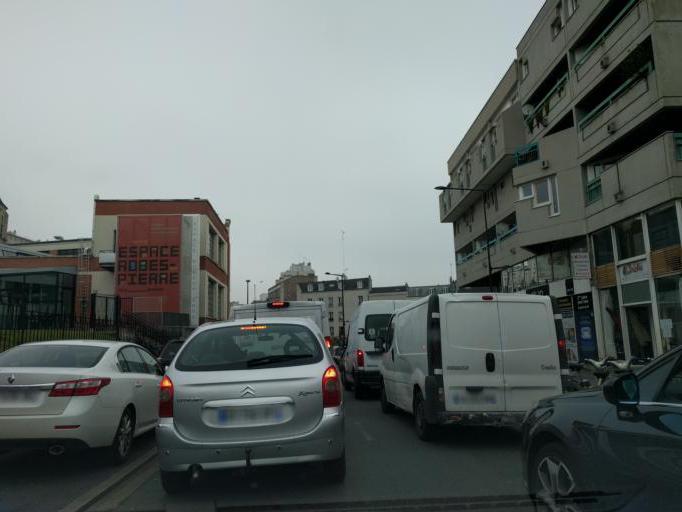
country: FR
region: Ile-de-France
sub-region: Departement du Val-de-Marne
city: Ivry-sur-Seine
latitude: 48.8106
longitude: 2.3842
